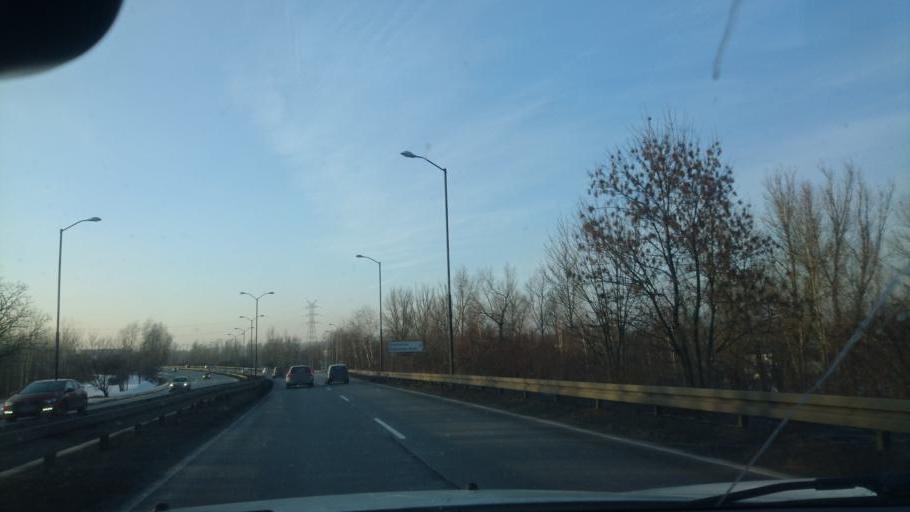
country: PL
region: Silesian Voivodeship
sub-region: Sosnowiec
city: Sosnowiec
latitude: 50.2577
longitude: 19.0785
